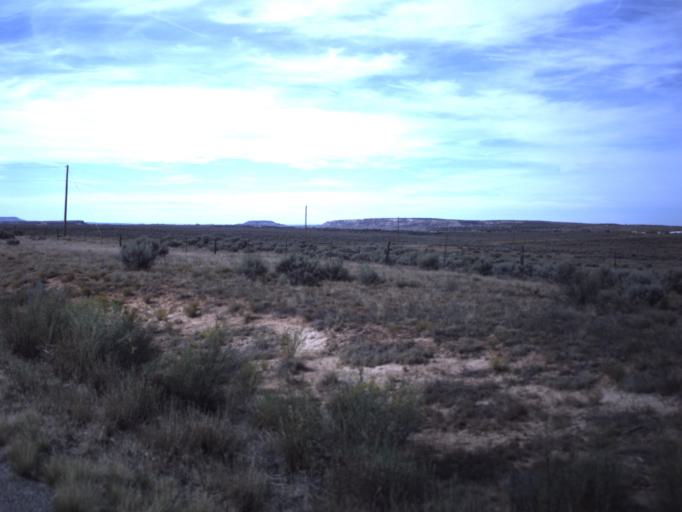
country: US
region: Utah
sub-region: San Juan County
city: Blanding
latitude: 37.4184
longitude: -109.3340
